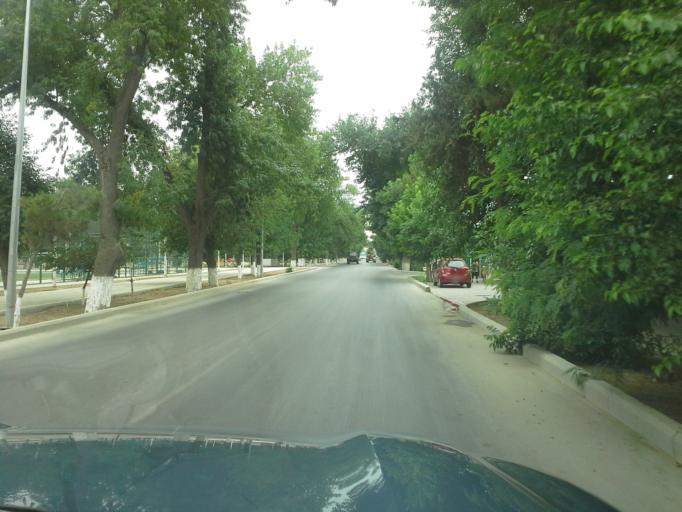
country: TM
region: Ahal
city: Ashgabat
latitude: 37.9523
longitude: 58.3636
